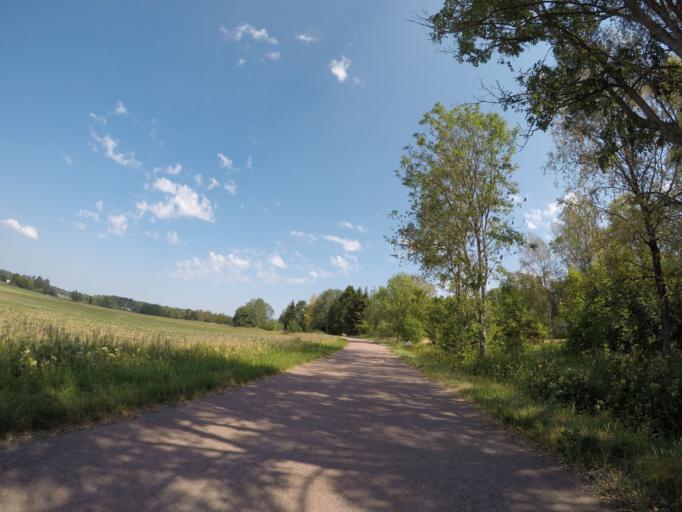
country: AX
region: Alands landsbygd
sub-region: Finstroem
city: Finstroem
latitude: 60.2084
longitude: 19.9030
